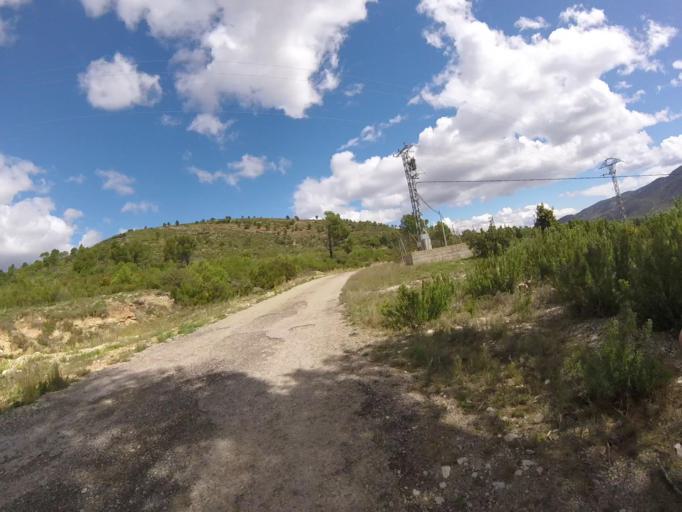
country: ES
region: Valencia
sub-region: Provincia de Castello
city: Sierra-Engarceran
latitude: 40.2750
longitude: -0.0812
